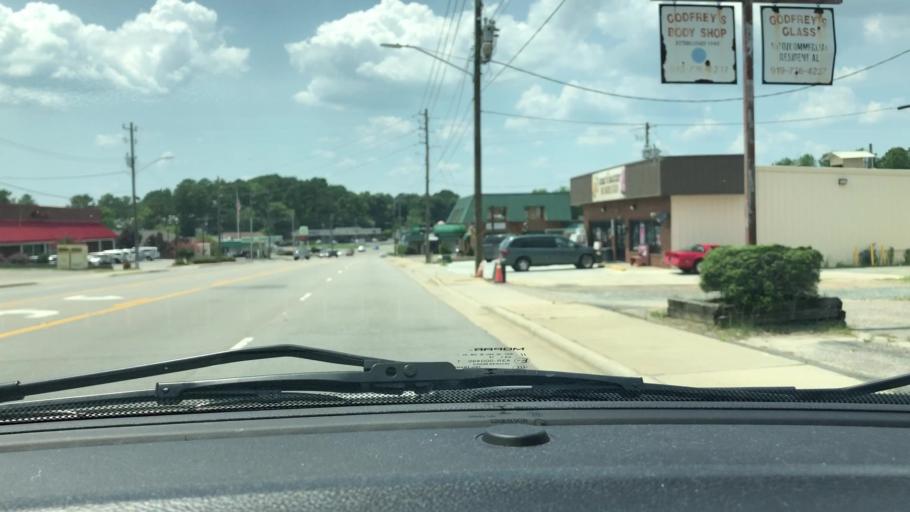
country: US
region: North Carolina
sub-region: Lee County
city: Sanford
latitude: 35.4706
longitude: -79.1696
